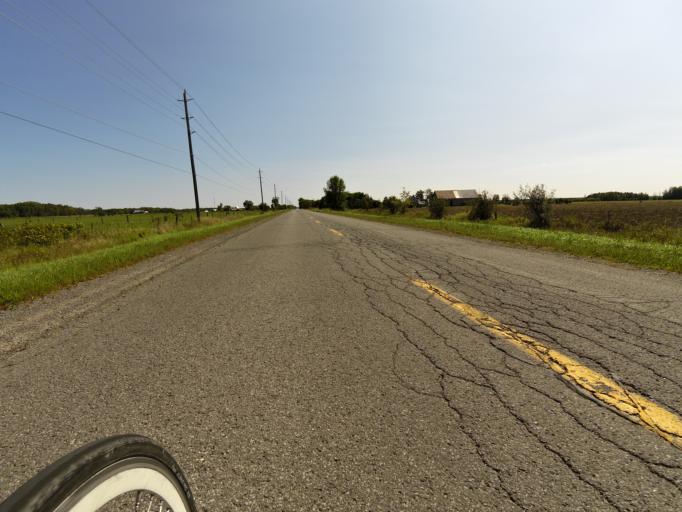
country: CA
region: Ontario
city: Arnprior
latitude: 45.4824
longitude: -76.1253
